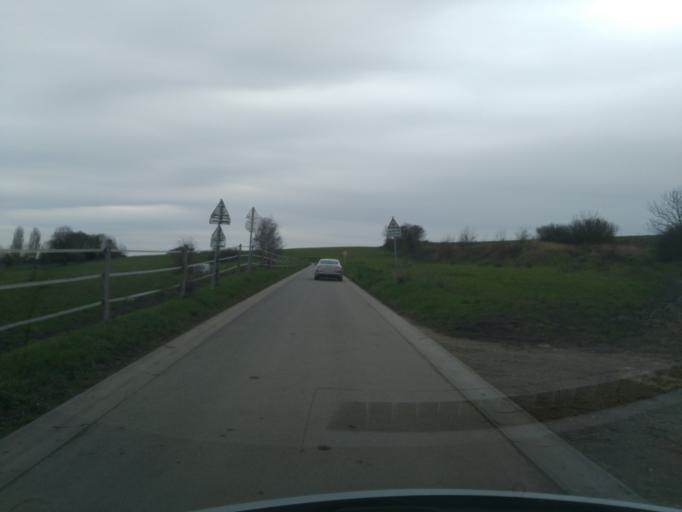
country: FR
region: Ile-de-France
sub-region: Departement des Yvelines
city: Chavenay
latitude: 48.8500
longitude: 1.9855
